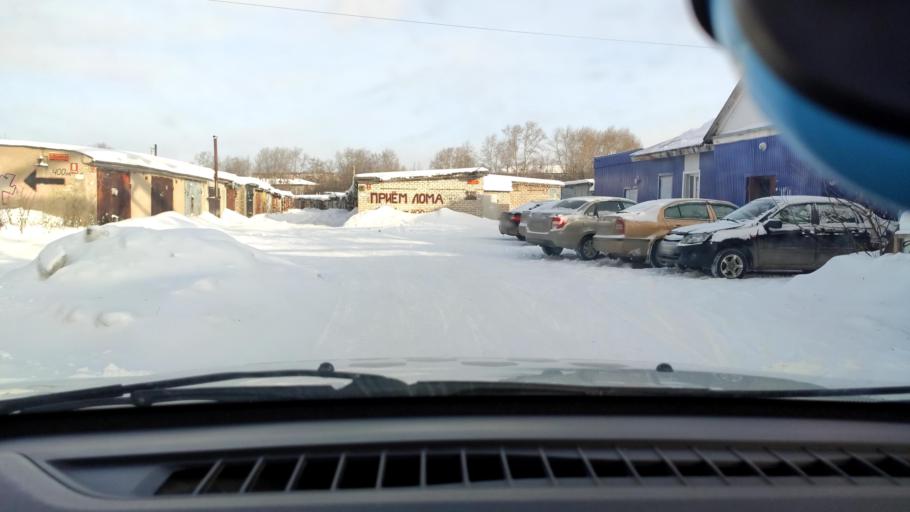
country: RU
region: Perm
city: Kultayevo
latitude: 57.9983
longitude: 55.9275
